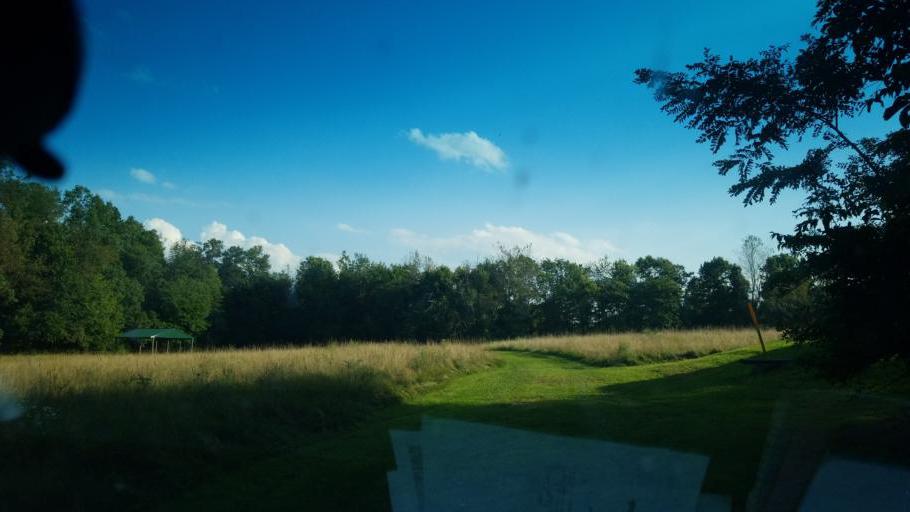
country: US
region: Ohio
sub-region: Sandusky County
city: Bellville
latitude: 40.5789
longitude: -82.4606
